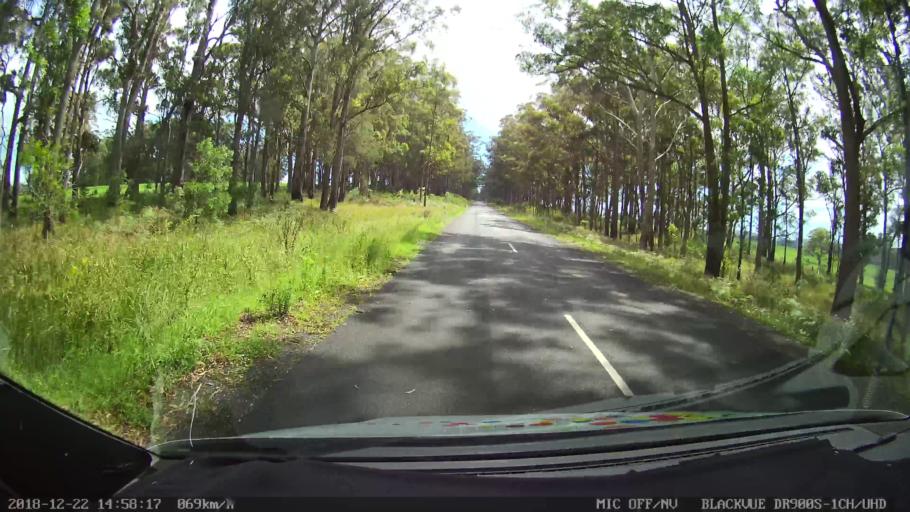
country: AU
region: New South Wales
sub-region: Bellingen
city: Dorrigo
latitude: -30.2392
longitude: 152.4926
